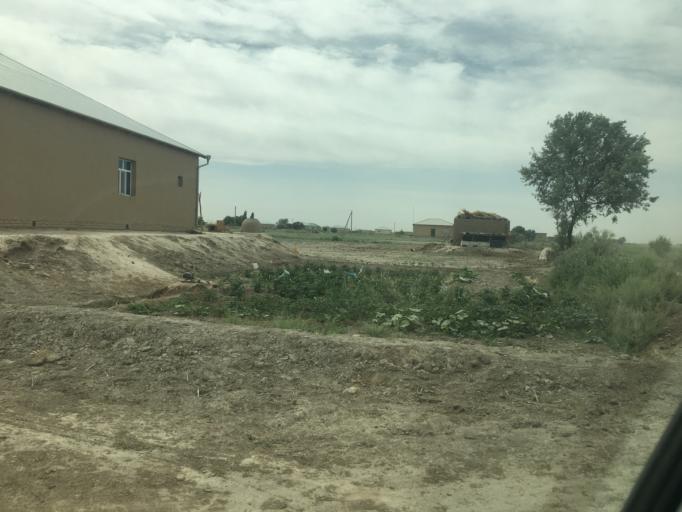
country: TM
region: Dasoguz
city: Tagta
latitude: 41.6145
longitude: 59.8178
